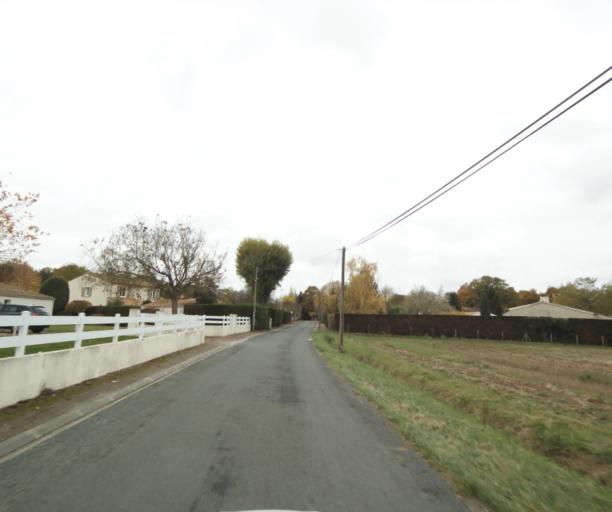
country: FR
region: Poitou-Charentes
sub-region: Departement de la Charente-Maritime
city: Saintes
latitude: 45.7651
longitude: -0.6390
